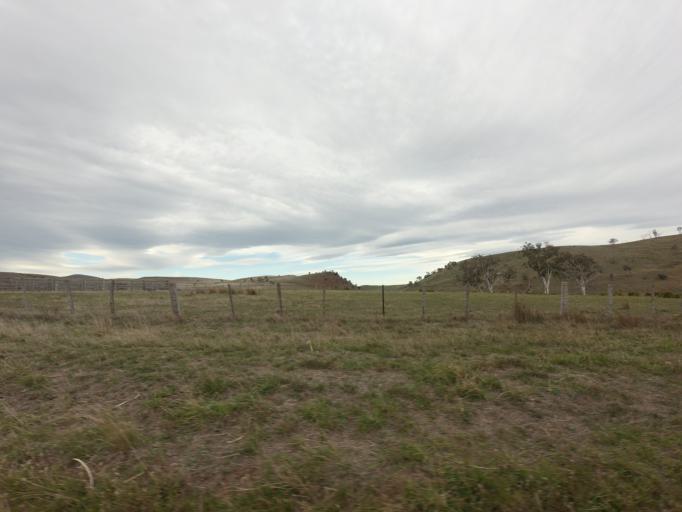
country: AU
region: Tasmania
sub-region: Derwent Valley
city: New Norfolk
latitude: -42.3700
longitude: 146.8463
